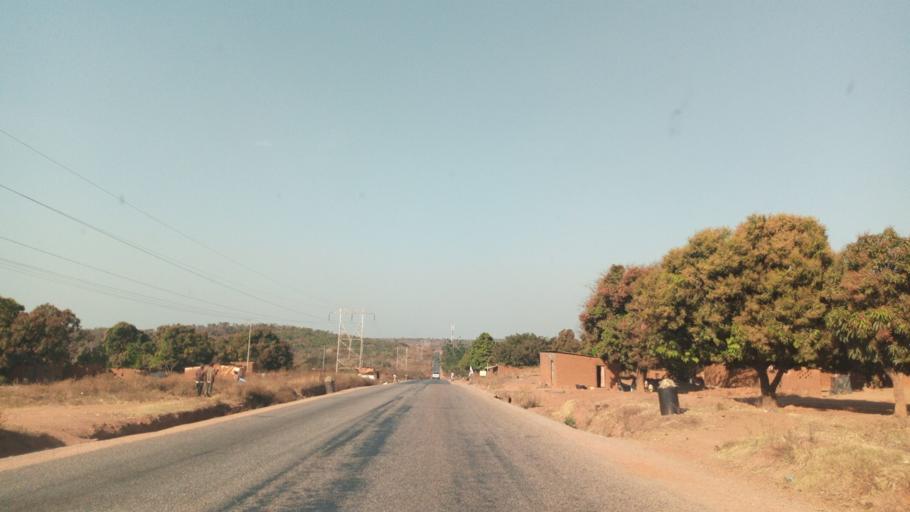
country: CD
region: Katanga
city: Likasi
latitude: -11.0005
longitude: 26.8819
